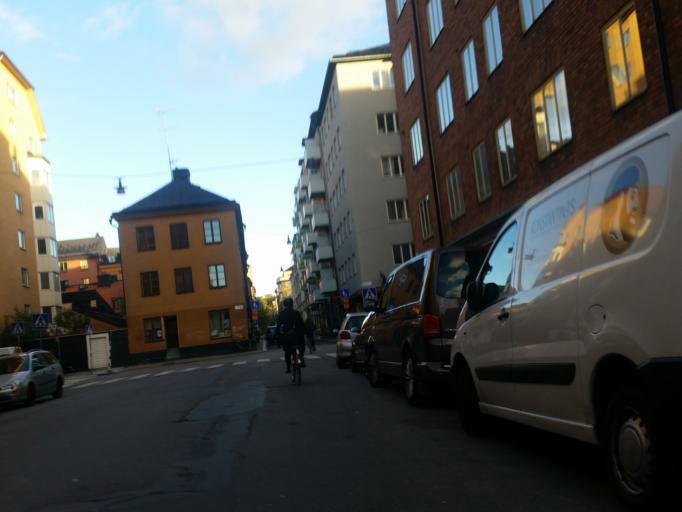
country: SE
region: Stockholm
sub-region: Stockholms Kommun
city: Stockholm
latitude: 59.3121
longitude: 18.0812
